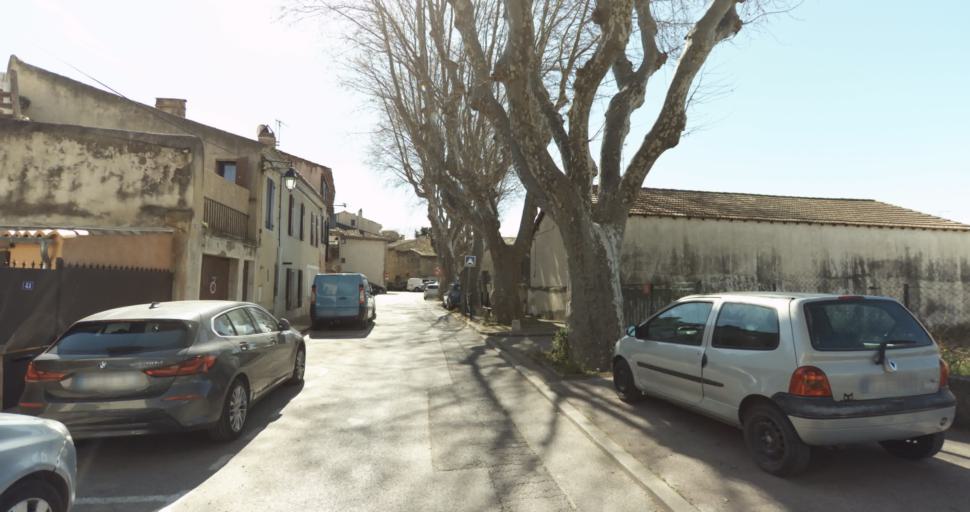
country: FR
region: Provence-Alpes-Cote d'Azur
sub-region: Departement des Bouches-du-Rhone
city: Lambesc
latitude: 43.6535
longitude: 5.2603
